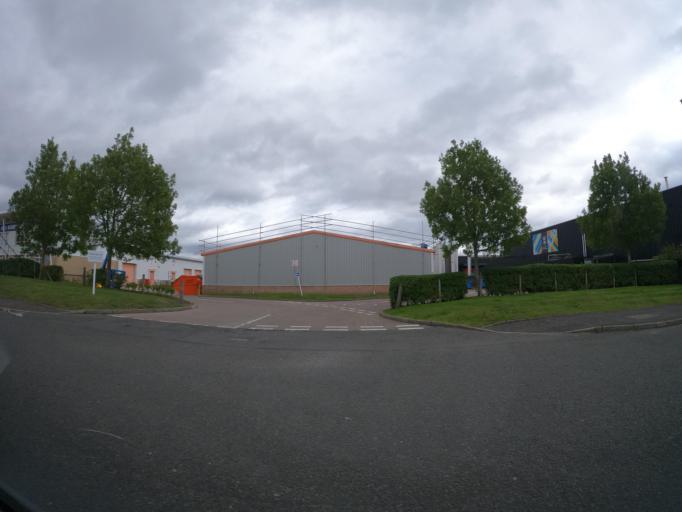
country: GB
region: Scotland
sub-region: Midlothian
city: Loanhead
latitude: 55.8730
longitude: -3.1623
